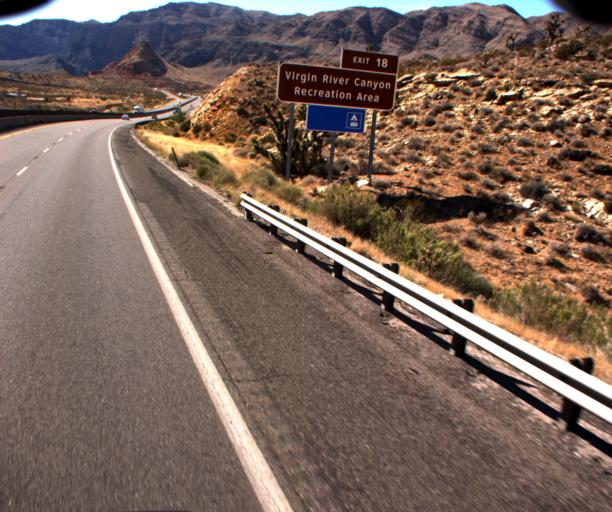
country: US
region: Arizona
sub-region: Mohave County
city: Beaver Dam
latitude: 36.9586
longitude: -113.7854
